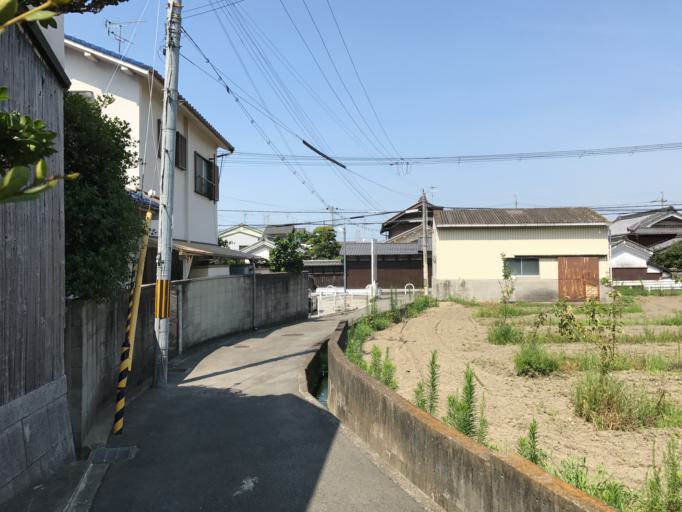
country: JP
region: Osaka
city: Kashihara
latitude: 34.6034
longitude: 135.6322
